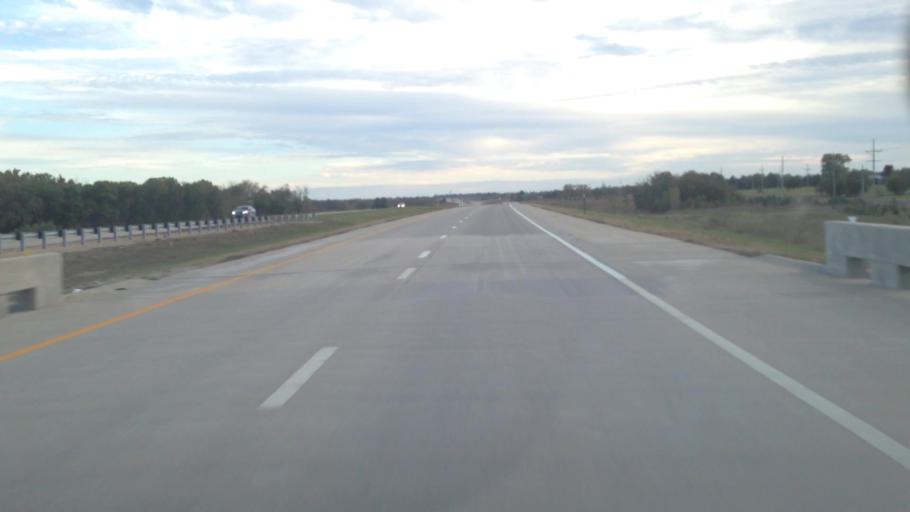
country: US
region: Kansas
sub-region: Douglas County
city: Baldwin City
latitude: 38.7385
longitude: -95.2678
